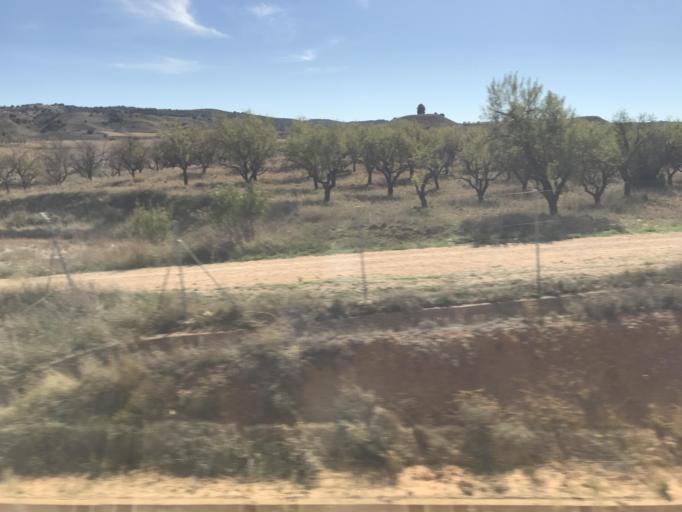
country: ES
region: Aragon
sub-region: Provincia de Zaragoza
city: Alhama de Aragon
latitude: 41.2794
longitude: -1.9131
